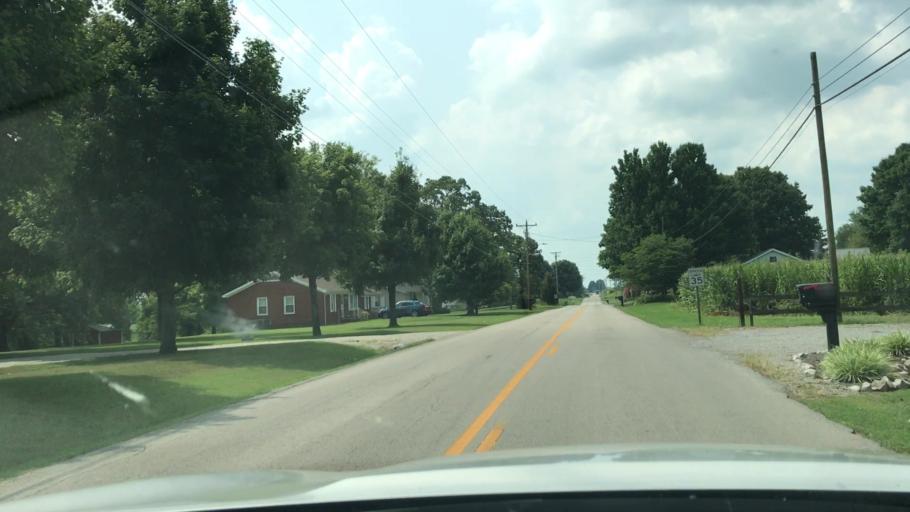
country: US
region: Kentucky
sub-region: Todd County
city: Elkton
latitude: 36.8013
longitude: -87.1488
